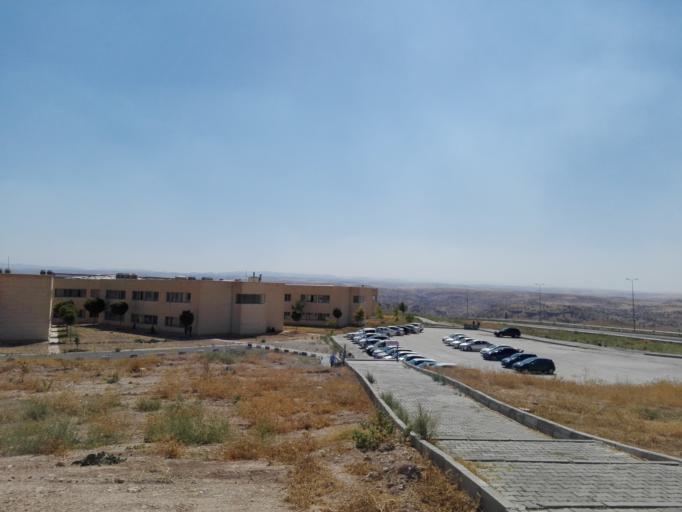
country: TR
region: Batman
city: Oymatas
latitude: 37.7865
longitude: 41.0627
